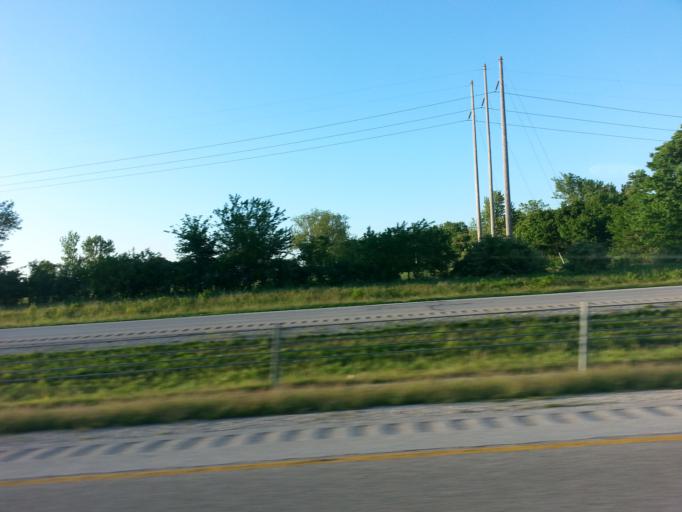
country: US
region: Illinois
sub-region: Vermilion County
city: Tilton
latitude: 40.1048
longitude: -87.6735
